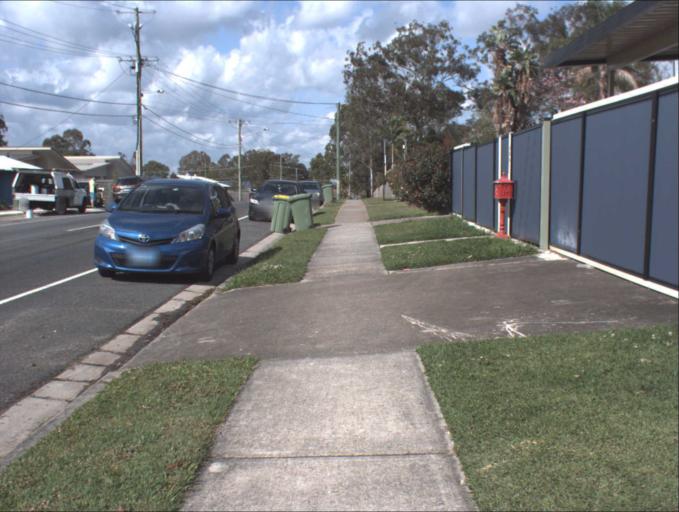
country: AU
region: Queensland
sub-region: Logan
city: Waterford West
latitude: -27.6850
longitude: 153.1330
